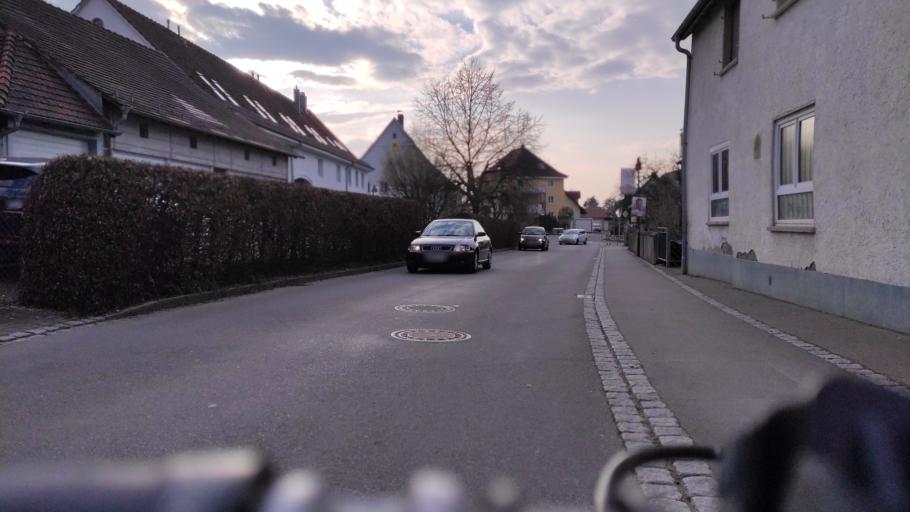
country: DE
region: Baden-Wuerttemberg
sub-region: Freiburg Region
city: Rielasingen-Worblingen
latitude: 47.7246
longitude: 8.8441
